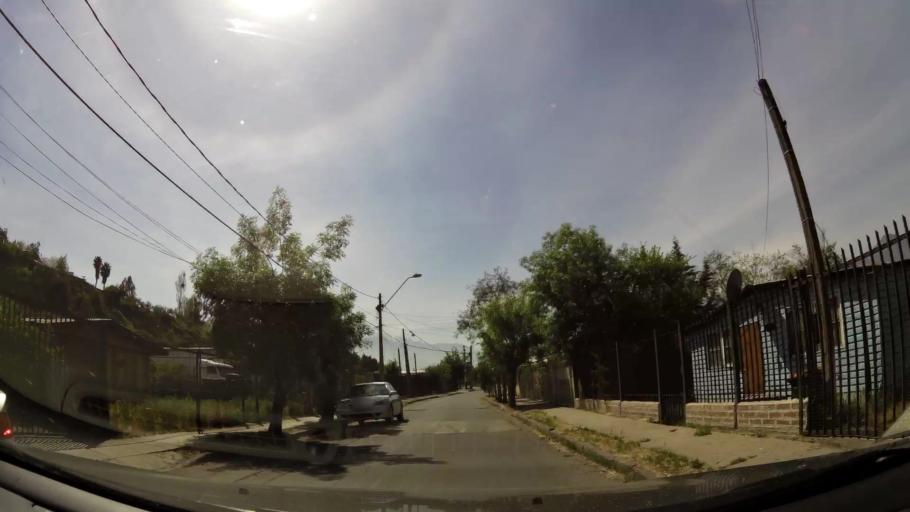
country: CL
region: Santiago Metropolitan
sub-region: Provincia de Cordillera
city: Puente Alto
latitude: -33.6278
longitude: -70.5801
